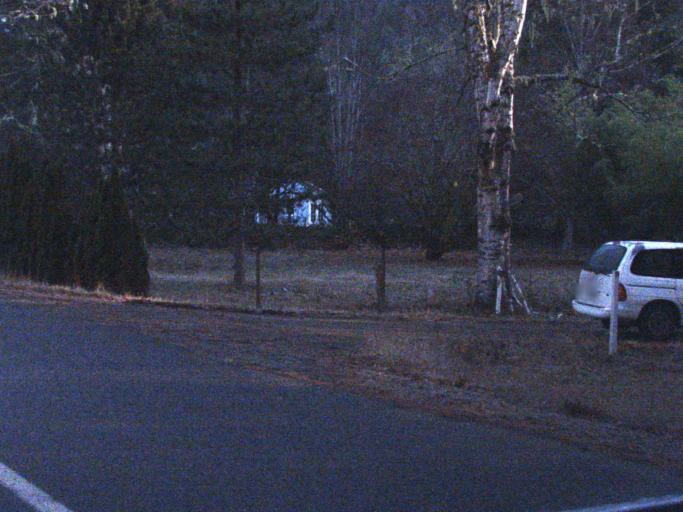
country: US
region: Washington
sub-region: Snohomish County
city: Darrington
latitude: 48.5589
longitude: -121.4161
